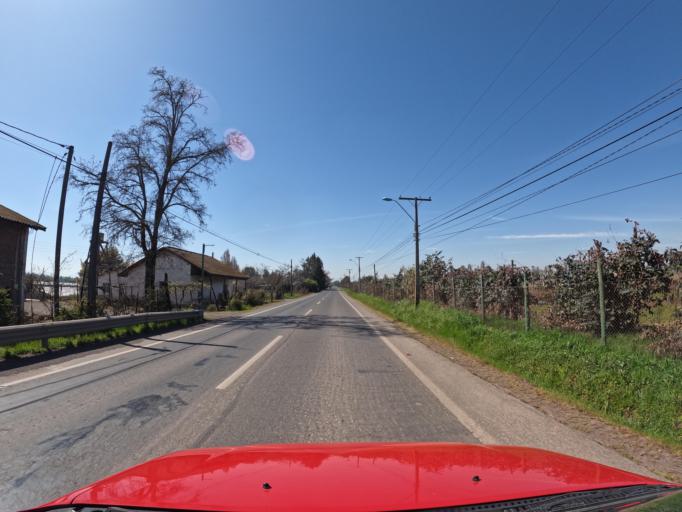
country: CL
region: Maule
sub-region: Provincia de Curico
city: Rauco
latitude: -34.9965
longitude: -71.3648
